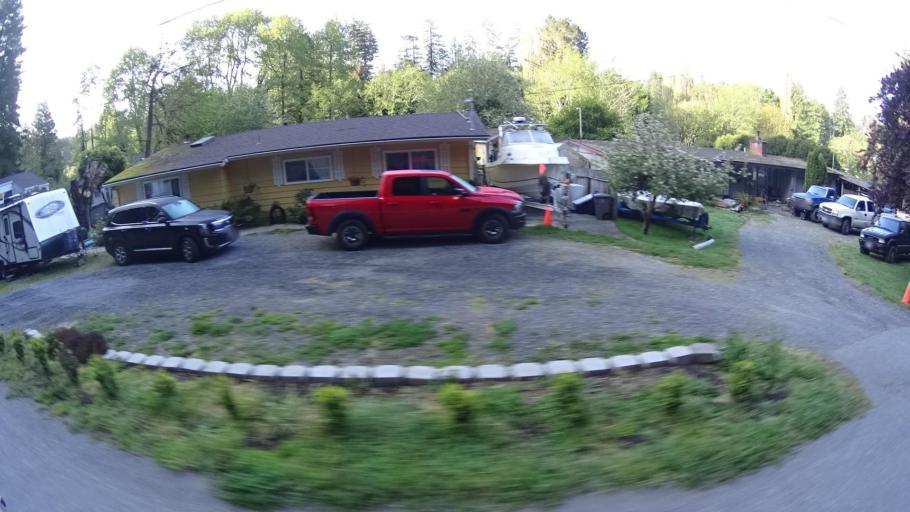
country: US
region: California
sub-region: Humboldt County
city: Myrtletown
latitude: 40.7603
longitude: -124.0542
